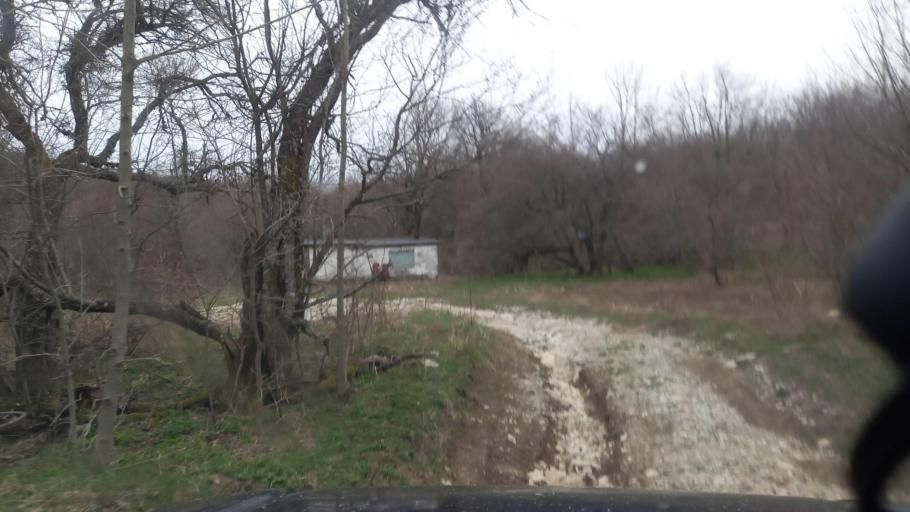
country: RU
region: Krasnodarskiy
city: Pshada
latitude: 44.5985
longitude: 38.2812
